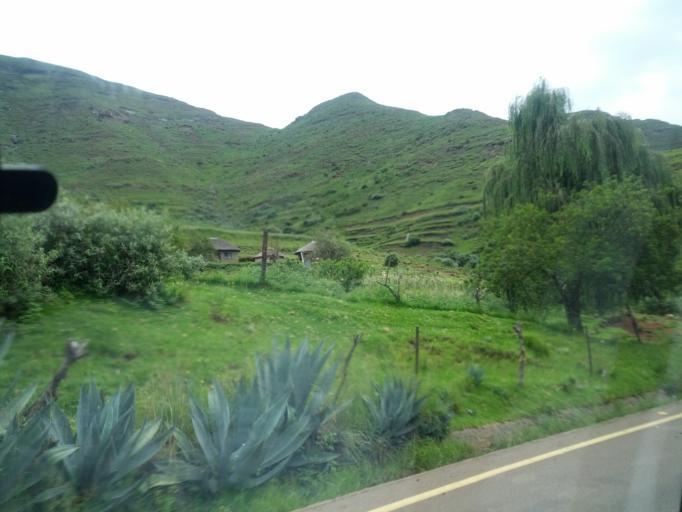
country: LS
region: Butha-Buthe
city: Butha-Buthe
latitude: -29.0429
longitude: 28.3074
